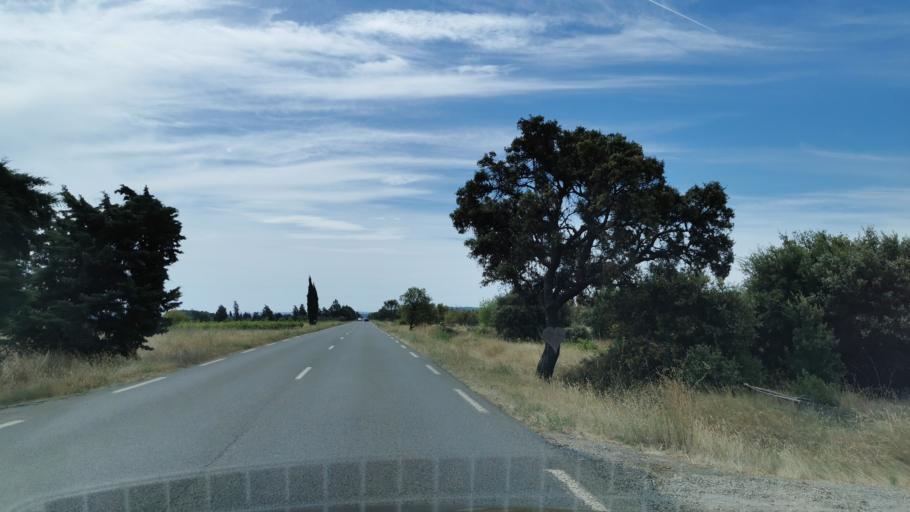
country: FR
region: Languedoc-Roussillon
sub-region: Departement de l'Aude
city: Ginestas
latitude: 43.2739
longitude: 2.8886
